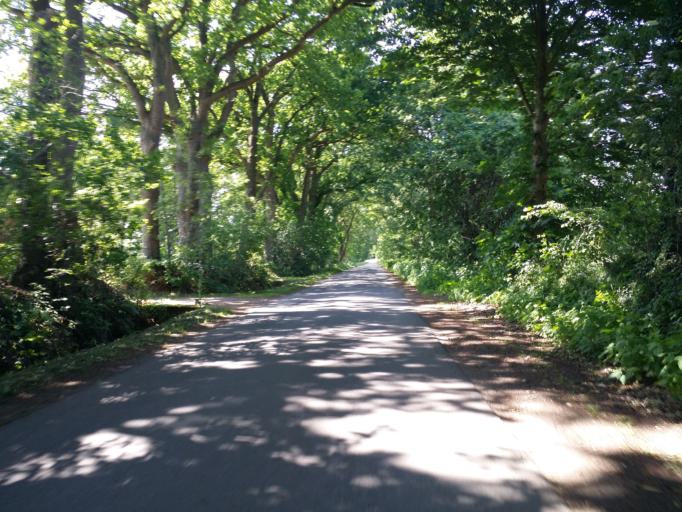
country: DE
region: Lower Saxony
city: Rastede
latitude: 53.2104
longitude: 8.2606
